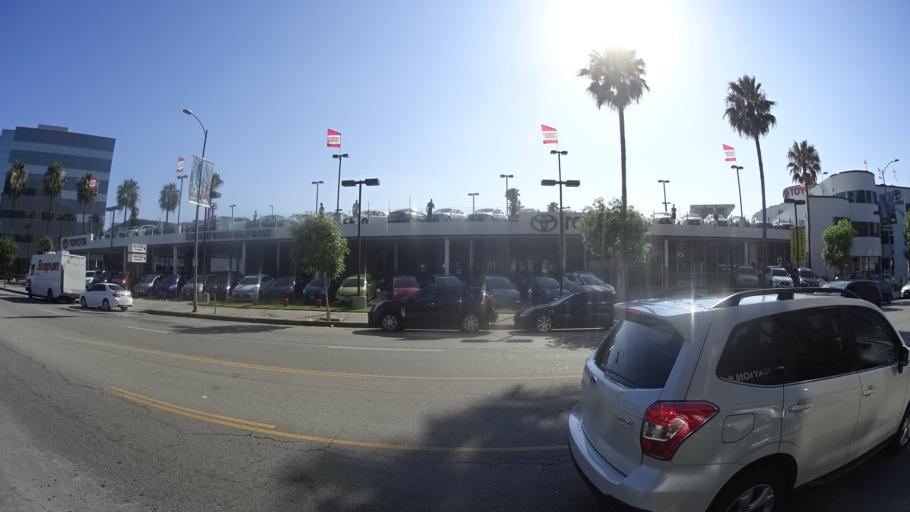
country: US
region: California
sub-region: Los Angeles County
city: North Hollywood
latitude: 34.1543
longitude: -118.3681
